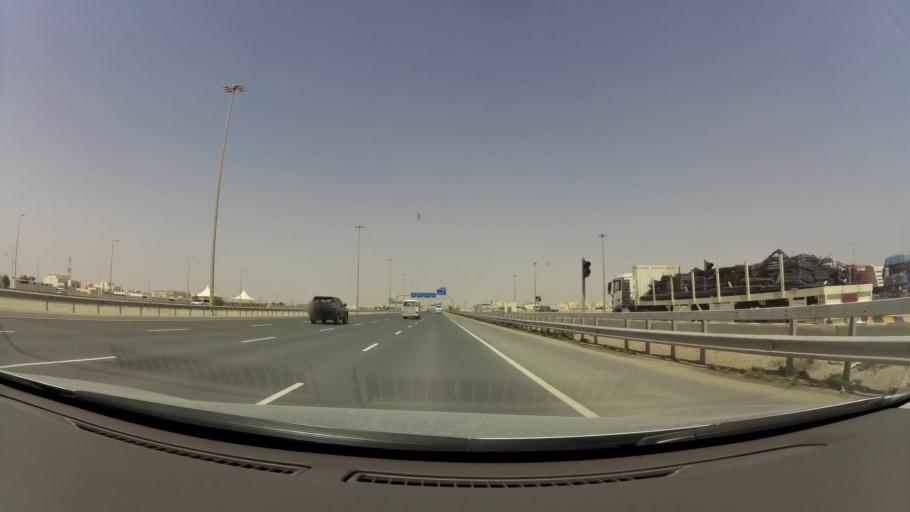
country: QA
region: Baladiyat Umm Salal
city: Umm Salal `Ali
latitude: 25.4684
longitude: 51.4085
